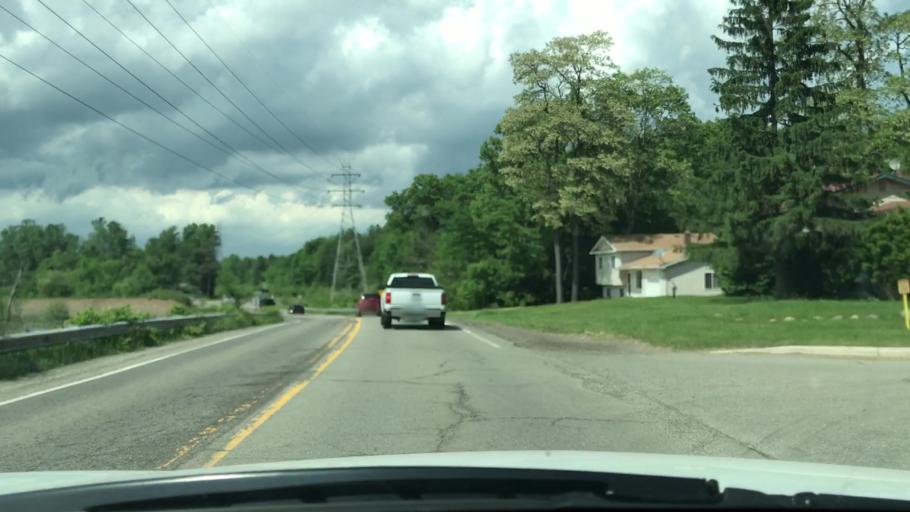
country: US
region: Michigan
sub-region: Oakland County
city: Auburn Hills
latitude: 42.7179
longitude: -83.2843
